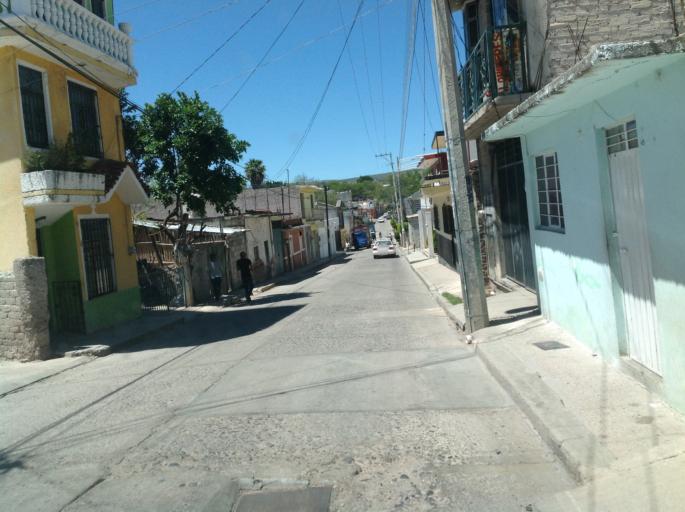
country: MX
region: Oaxaca
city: Ciudad de Huajuapam de Leon
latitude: 17.8127
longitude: -97.7763
